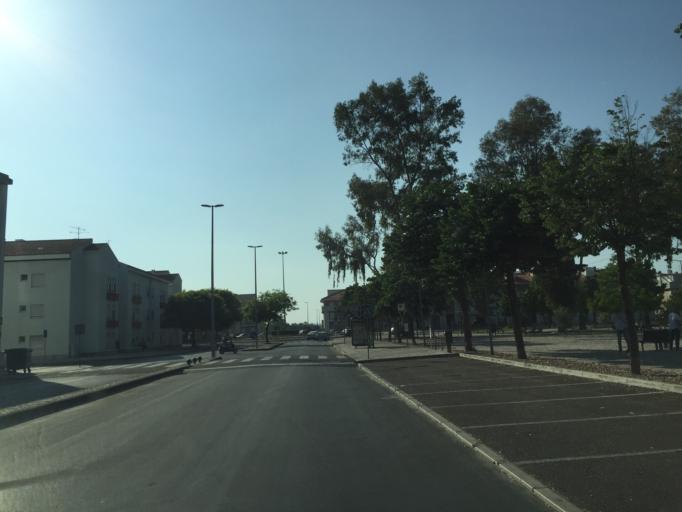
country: PT
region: Santarem
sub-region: Almeirim
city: Almeirim
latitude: 39.2140
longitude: -8.6217
